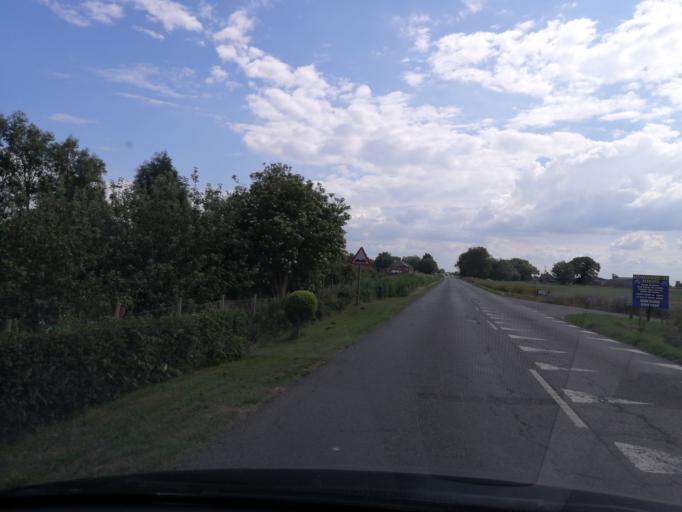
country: GB
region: England
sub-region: Cambridgeshire
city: Whittlesey
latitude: 52.5089
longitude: -0.1439
